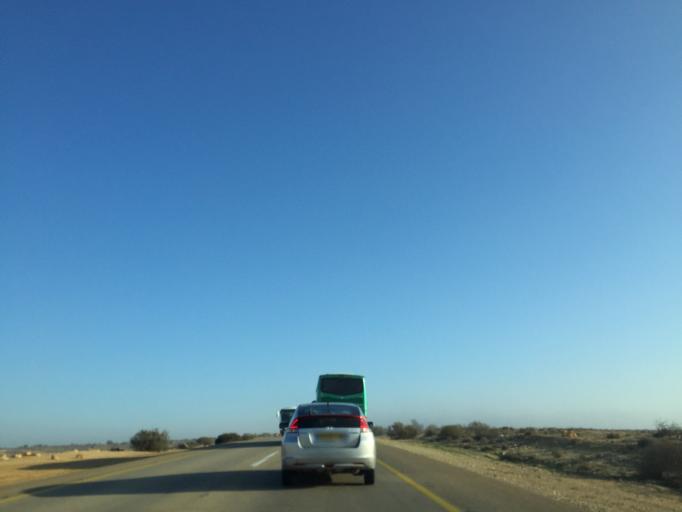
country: IL
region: Southern District
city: Yeroham
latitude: 31.0221
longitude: 34.9658
